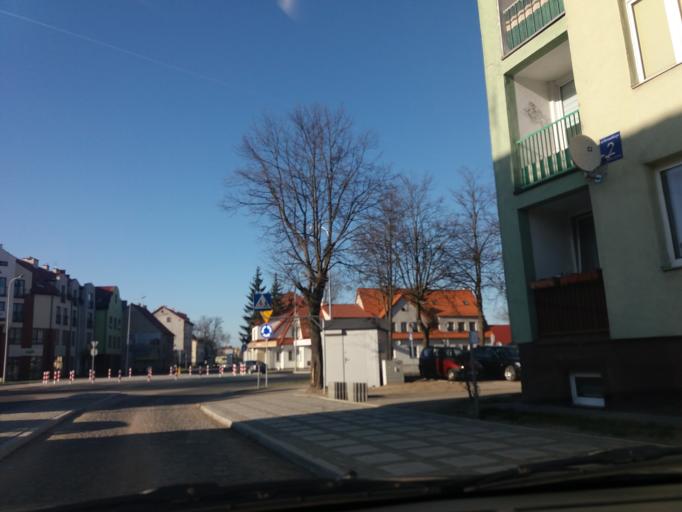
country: PL
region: Warmian-Masurian Voivodeship
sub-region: Powiat nidzicki
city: Nidzica
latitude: 53.3610
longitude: 20.4259
